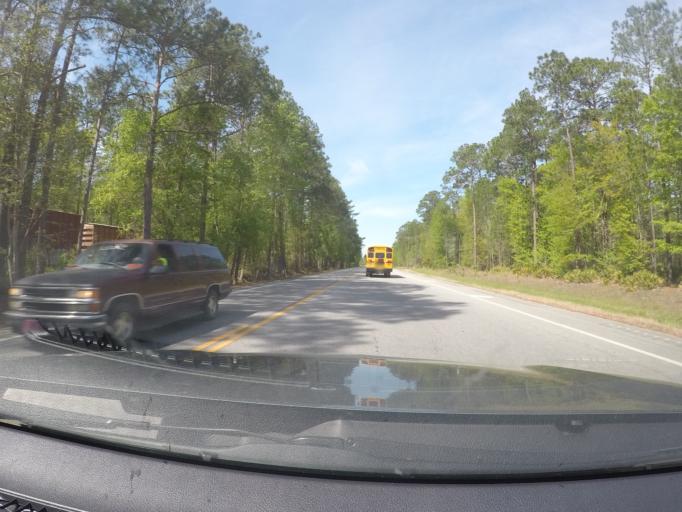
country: US
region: Georgia
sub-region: Bryan County
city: Pembroke
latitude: 32.1306
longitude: -81.5480
